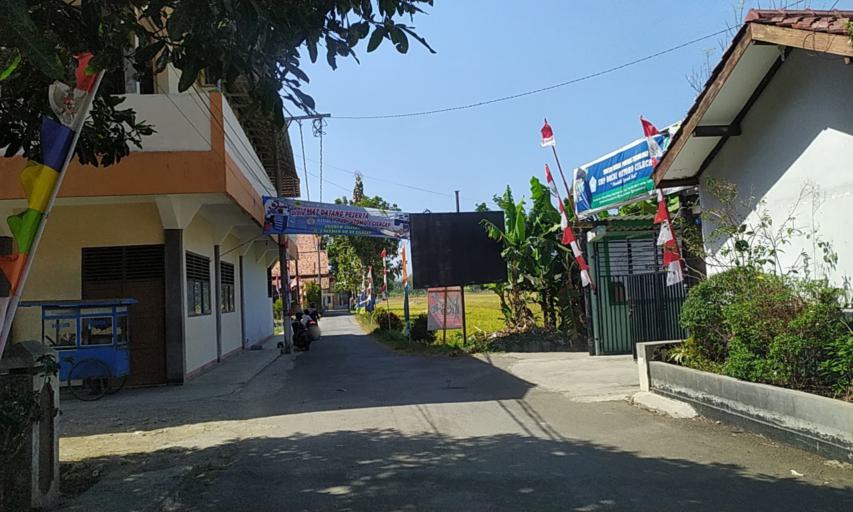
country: ID
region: Central Java
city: Karangbadar Kidul
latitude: -7.7001
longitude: 109.0328
